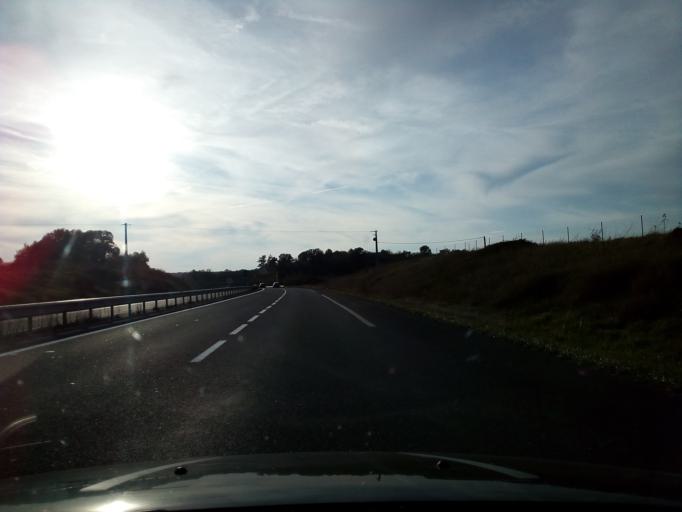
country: FR
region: Poitou-Charentes
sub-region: Departement de la Charente
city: Saint-Projet-Saint-Constant
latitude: 45.7403
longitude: 0.3498
